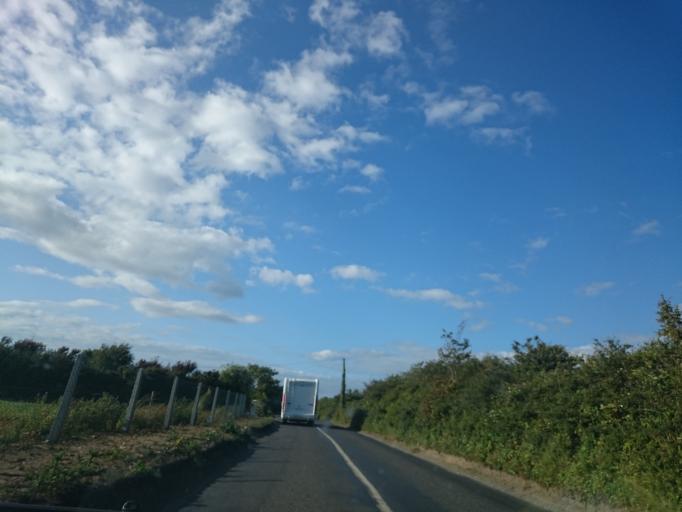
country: IE
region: Leinster
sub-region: Loch Garman
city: Loch Garman
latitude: 52.1962
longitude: -6.5576
